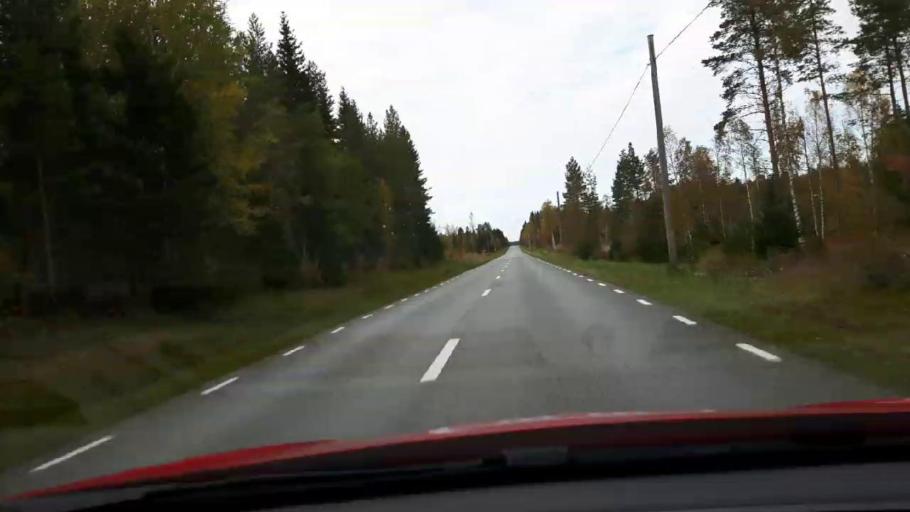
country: SE
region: Jaemtland
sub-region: Krokoms Kommun
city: Krokom
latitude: 63.1930
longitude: 14.0543
